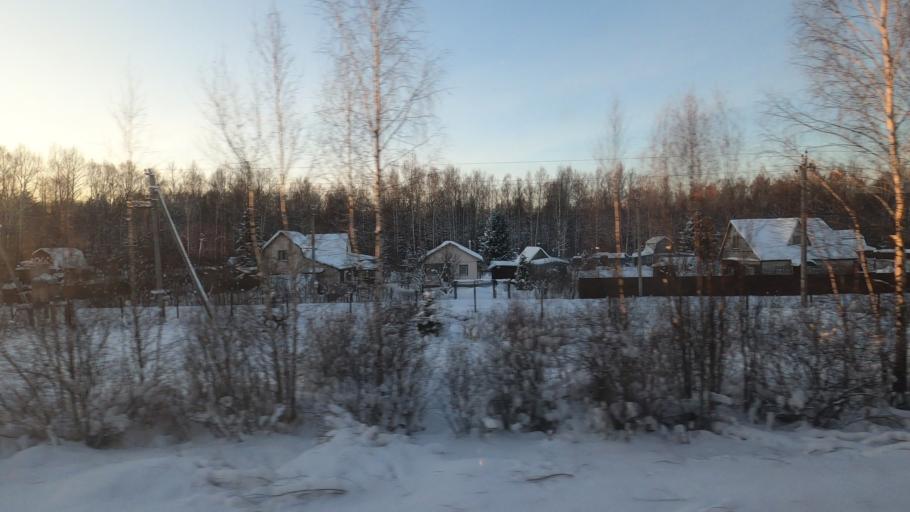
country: RU
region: Moskovskaya
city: Orud'yevo
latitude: 56.4299
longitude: 37.4997
